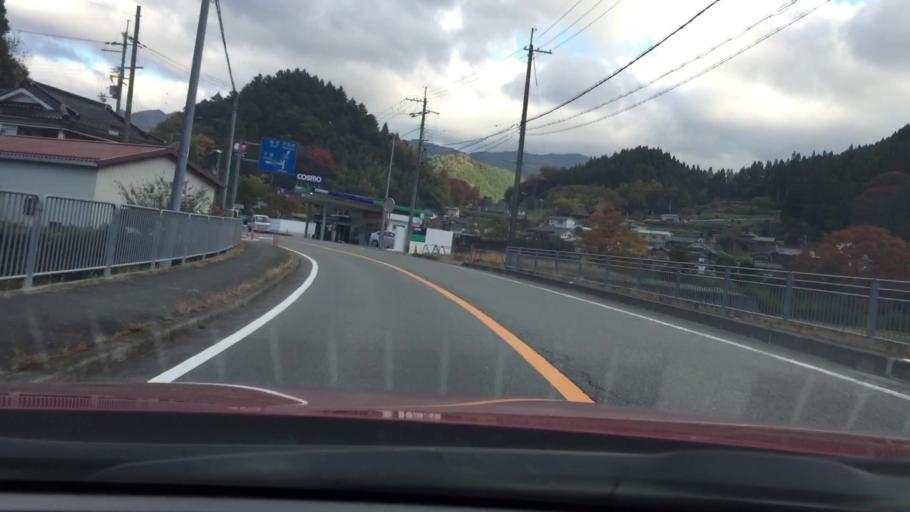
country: JP
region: Hyogo
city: Yamazakicho-nakabirose
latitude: 35.1568
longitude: 134.5457
